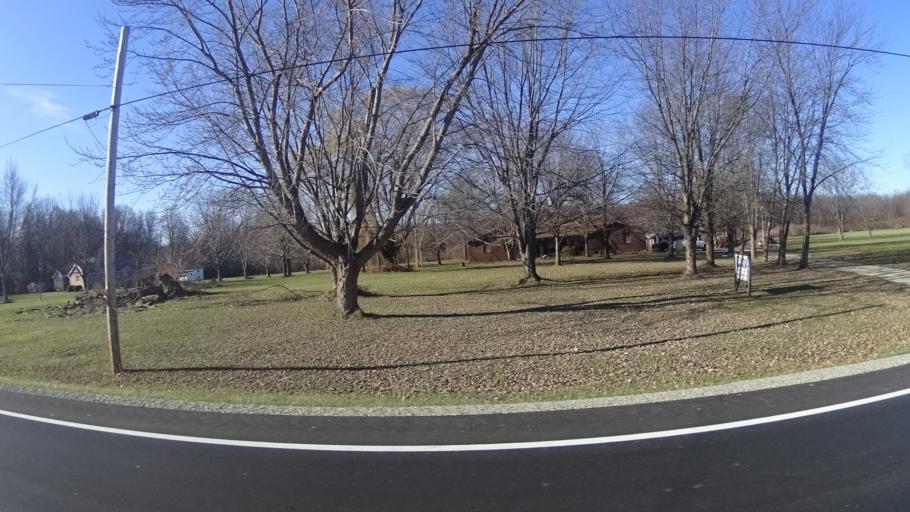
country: US
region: Ohio
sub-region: Lorain County
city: South Amherst
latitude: 41.3555
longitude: -82.2769
